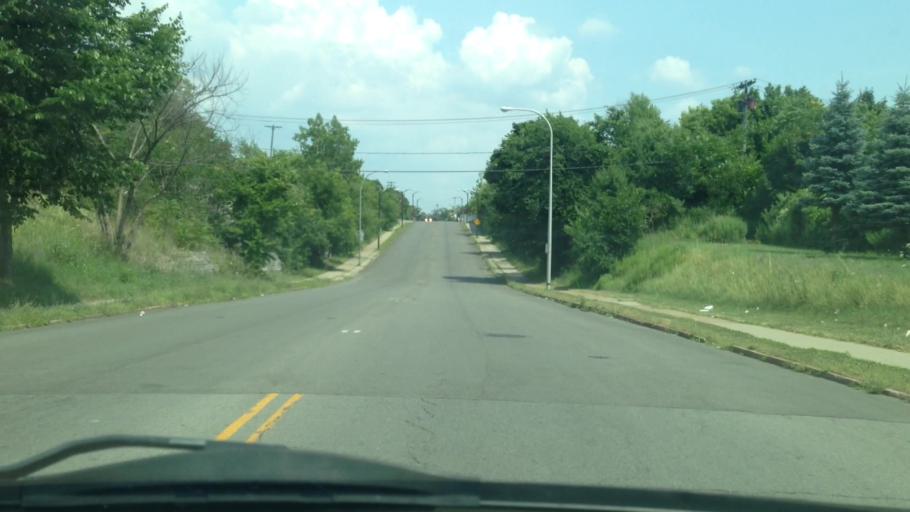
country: US
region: New York
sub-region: Erie County
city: Eggertsville
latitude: 42.9401
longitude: -78.8280
